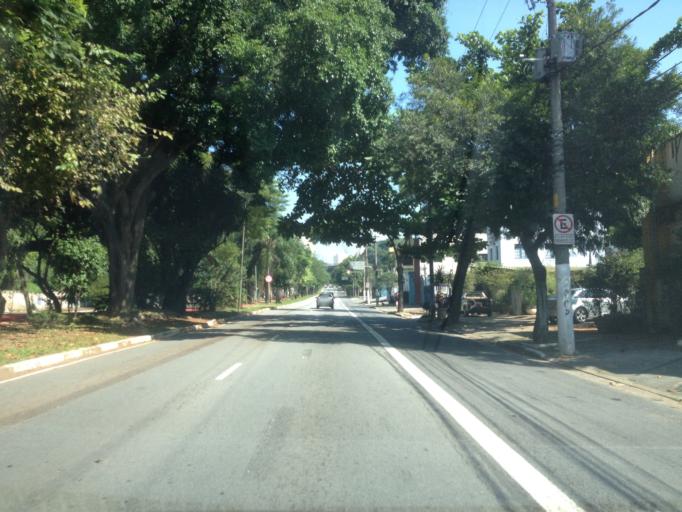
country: BR
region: Sao Paulo
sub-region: Sao Paulo
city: Sao Paulo
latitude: -23.5449
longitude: -46.6768
